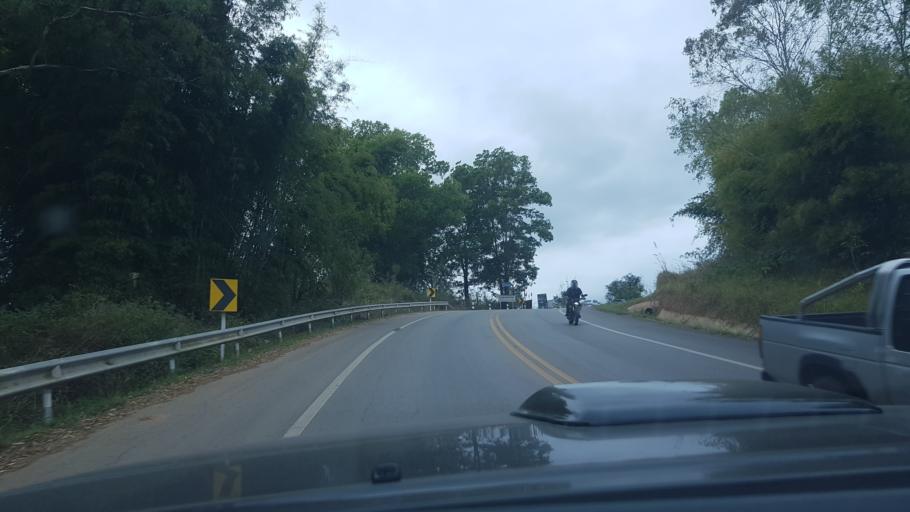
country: TH
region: Phetchabun
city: Khao Kho
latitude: 16.5613
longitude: 101.0110
